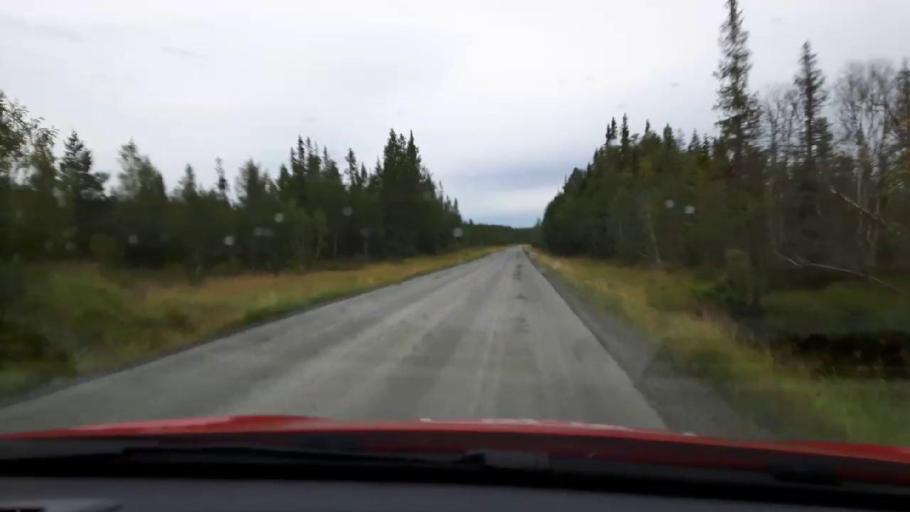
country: SE
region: Jaemtland
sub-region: Are Kommun
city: Are
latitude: 63.4407
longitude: 13.2507
